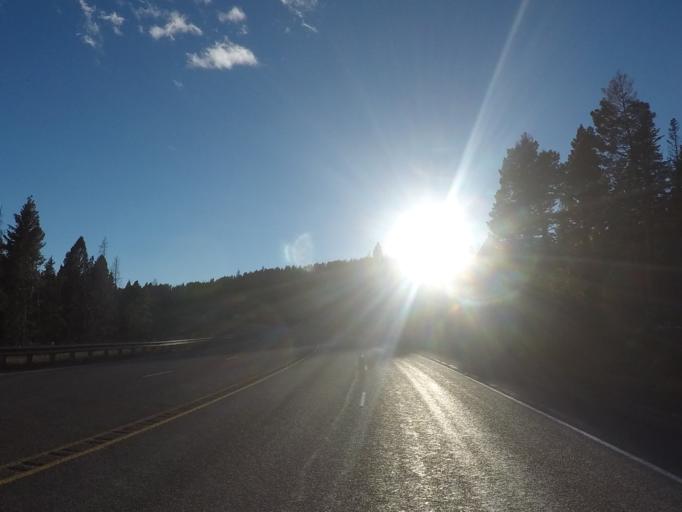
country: US
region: Montana
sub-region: Lewis and Clark County
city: Helena West Side
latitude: 46.5743
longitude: -112.2976
